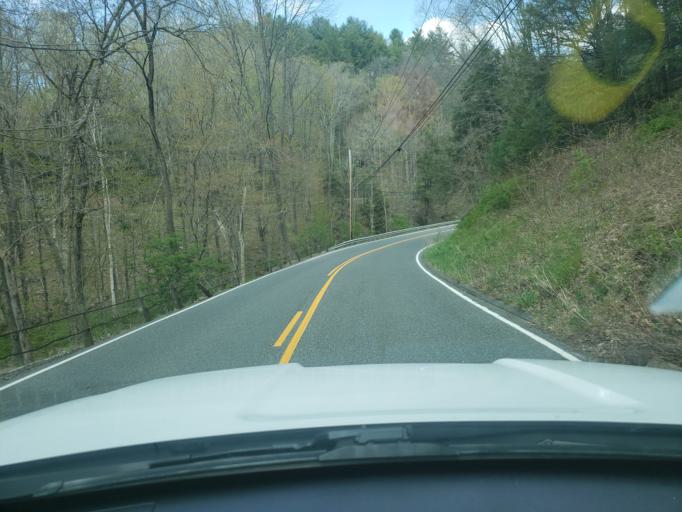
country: US
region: Connecticut
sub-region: Litchfield County
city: New Milford
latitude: 41.5917
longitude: -73.3216
